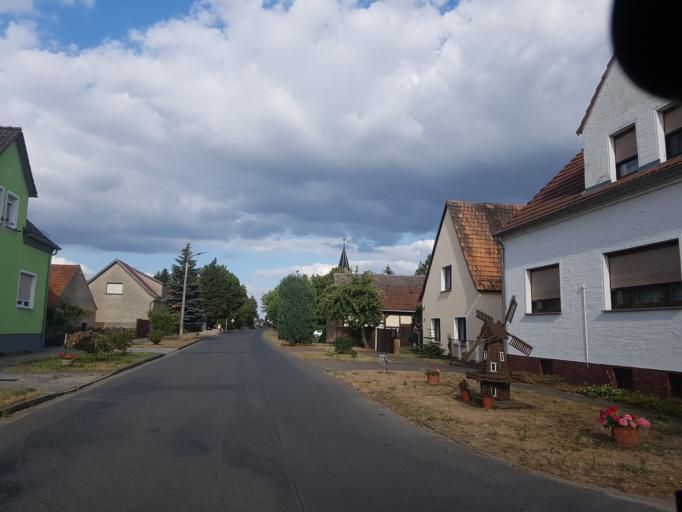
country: DE
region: Brandenburg
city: Herzberg
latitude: 51.7609
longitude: 13.2555
